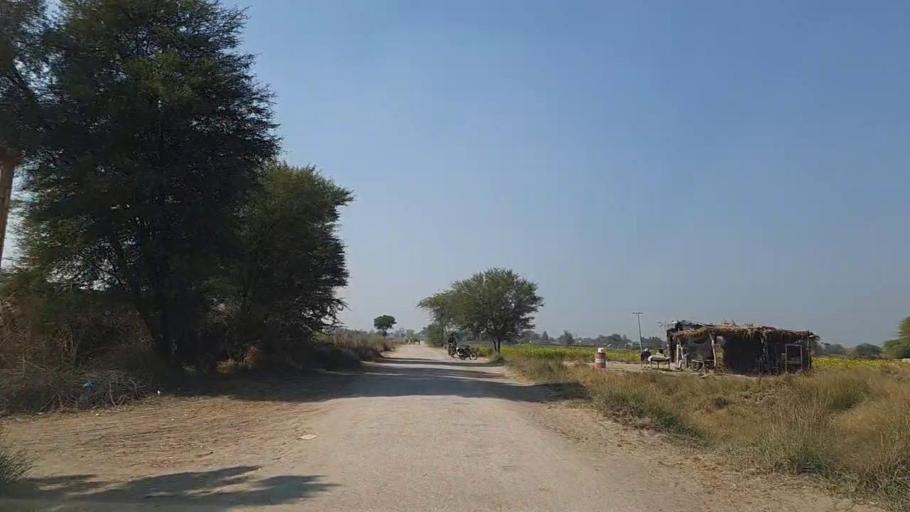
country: PK
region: Sindh
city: Daur
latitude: 26.5030
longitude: 68.3302
